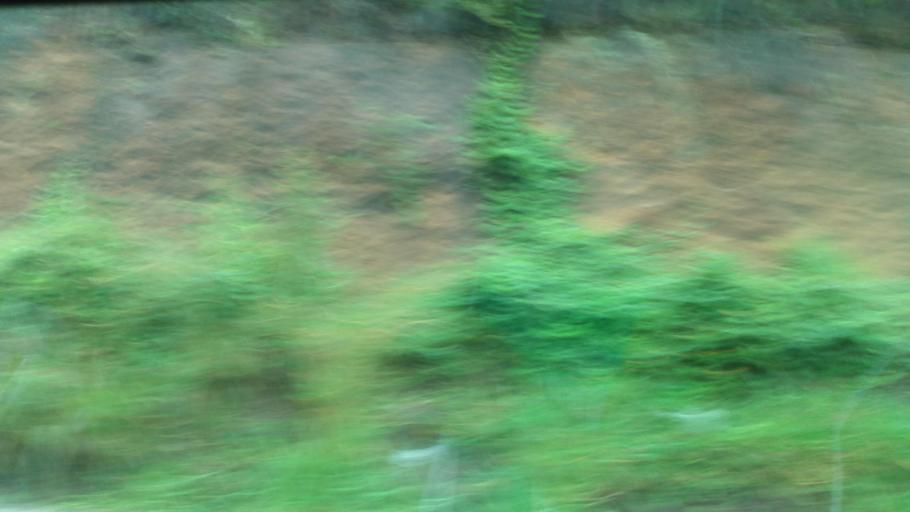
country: BR
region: Pernambuco
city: Garanhuns
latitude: -8.8763
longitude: -36.5169
